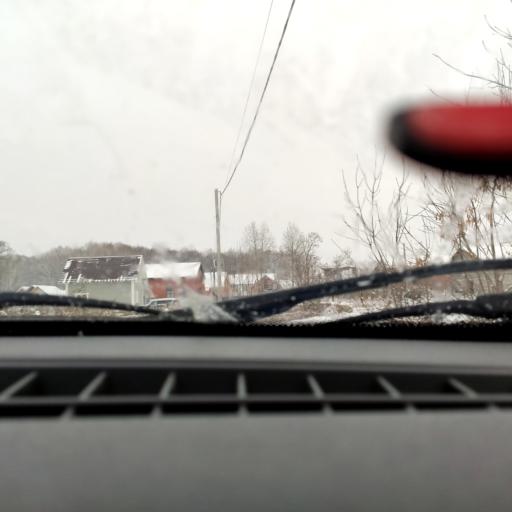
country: RU
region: Bashkortostan
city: Ufa
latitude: 54.6266
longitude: 55.8843
